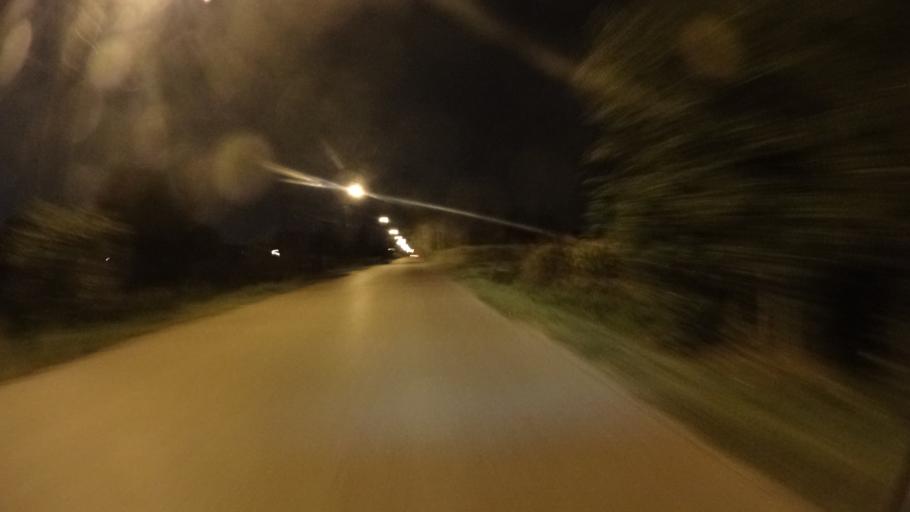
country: PL
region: Masovian Voivodeship
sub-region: Powiat warszawski zachodni
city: Hornowek
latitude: 52.2506
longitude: 20.7894
